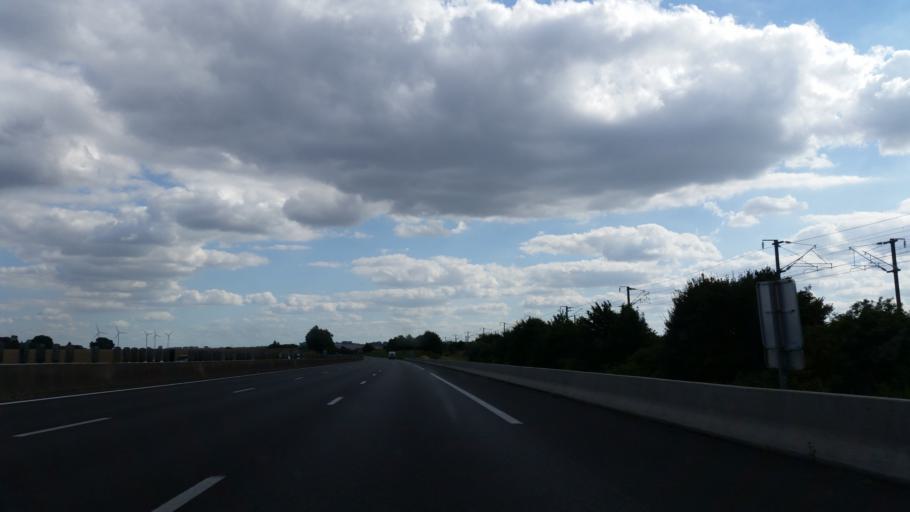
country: FR
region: Nord-Pas-de-Calais
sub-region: Departement du Pas-de-Calais
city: Bapaume
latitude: 50.0856
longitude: 2.8702
